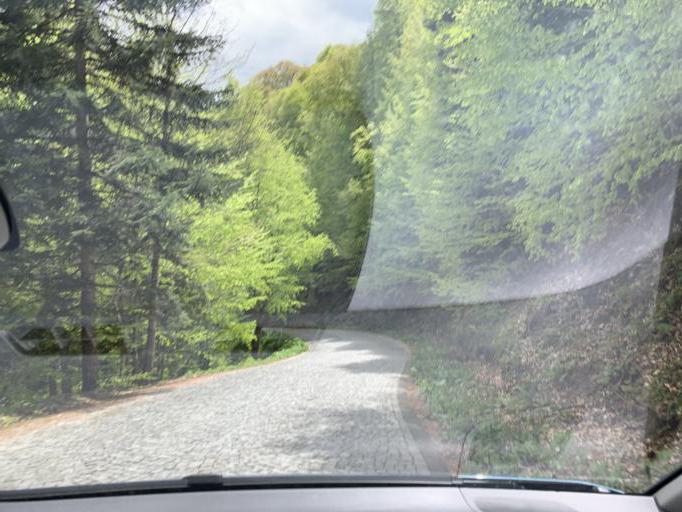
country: TR
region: Zonguldak
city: Egerci
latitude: 40.9293
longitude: 31.7461
